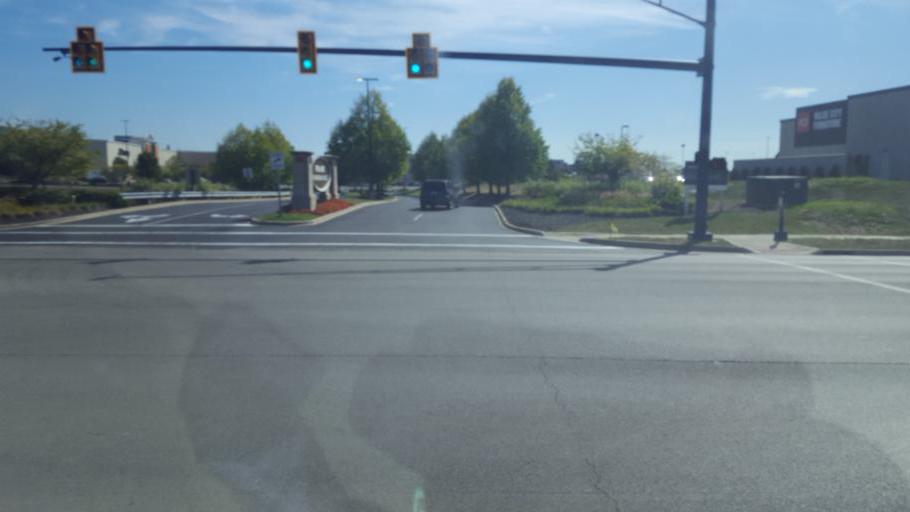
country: US
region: Ohio
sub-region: Delaware County
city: Lewis Center
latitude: 40.1486
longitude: -82.9843
